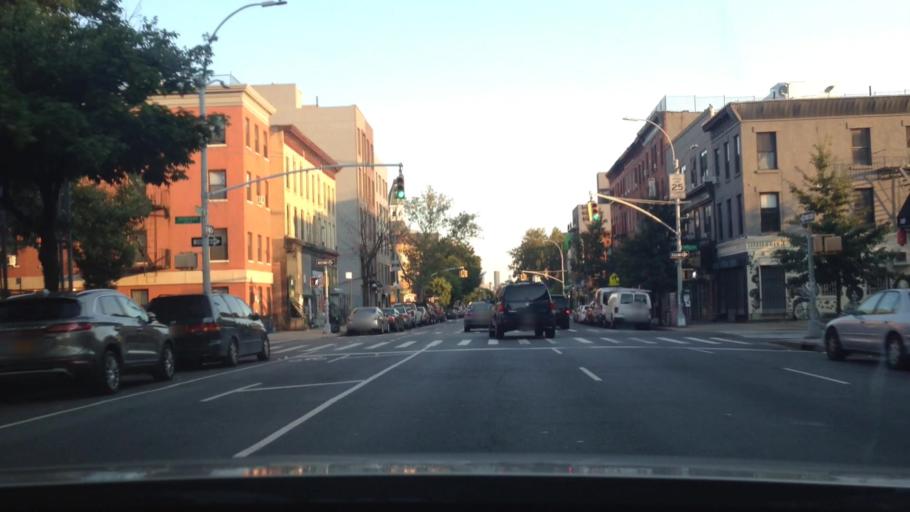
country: US
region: New York
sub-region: Kings County
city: Brooklyn
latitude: 40.6825
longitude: -73.9538
